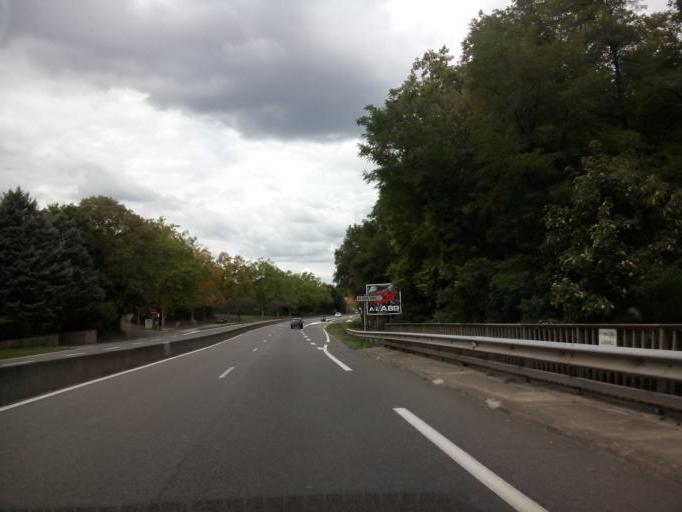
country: FR
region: Rhone-Alpes
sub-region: Departement du Rhone
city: Lissieu
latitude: 45.8401
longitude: 4.7390
